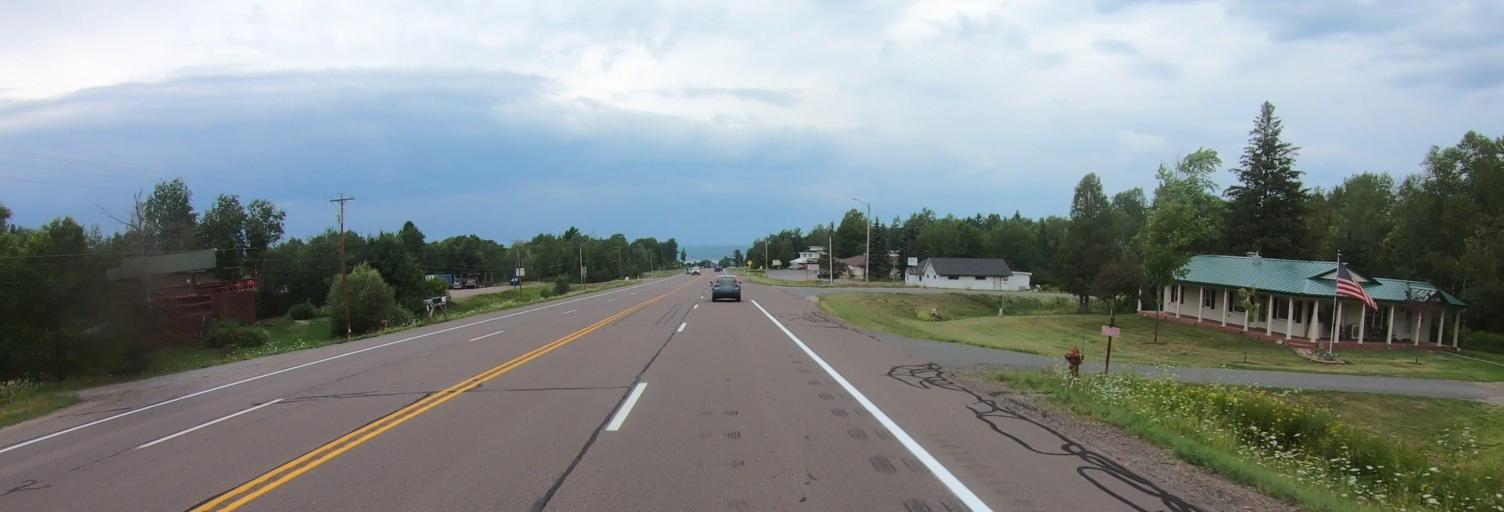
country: US
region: Michigan
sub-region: Baraga County
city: L'Anse
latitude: 46.7442
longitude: -88.4350
